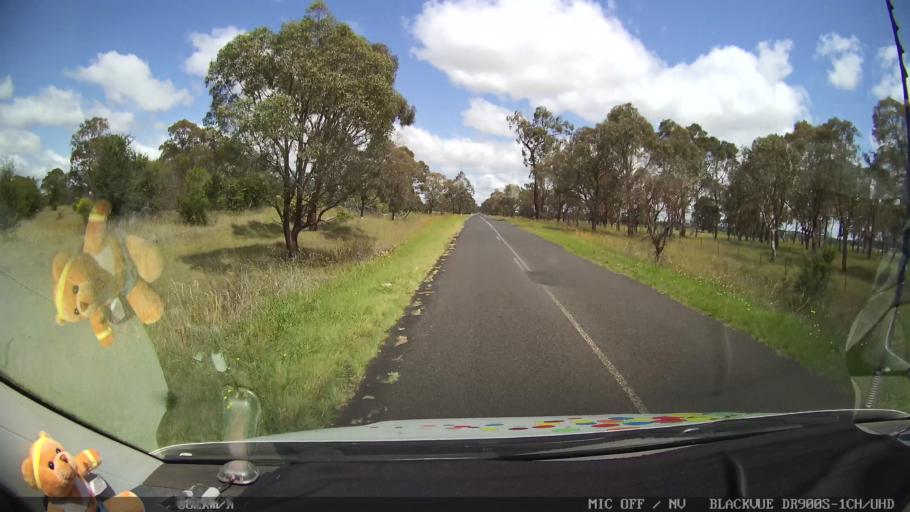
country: AU
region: New South Wales
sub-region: Glen Innes Severn
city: Glen Innes
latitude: -29.6367
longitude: 151.6839
